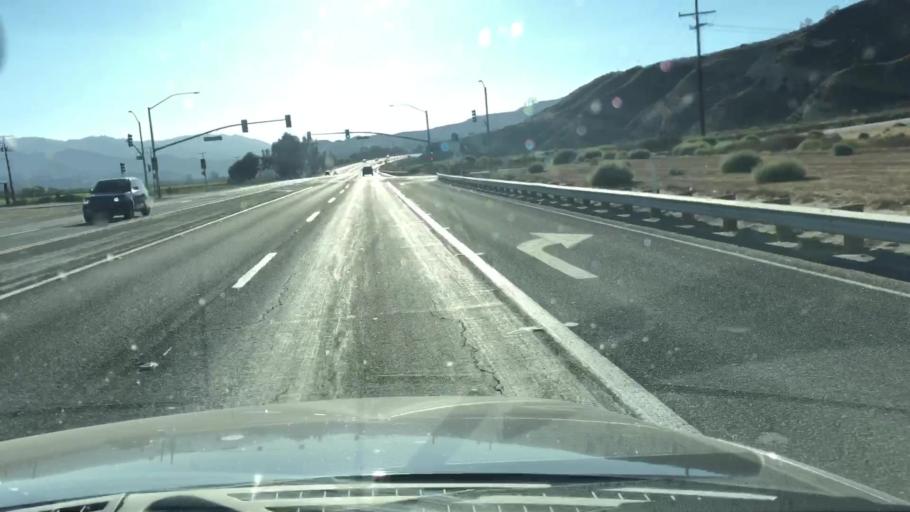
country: US
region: California
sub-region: Los Angeles County
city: Val Verde
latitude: 34.4259
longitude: -118.6368
